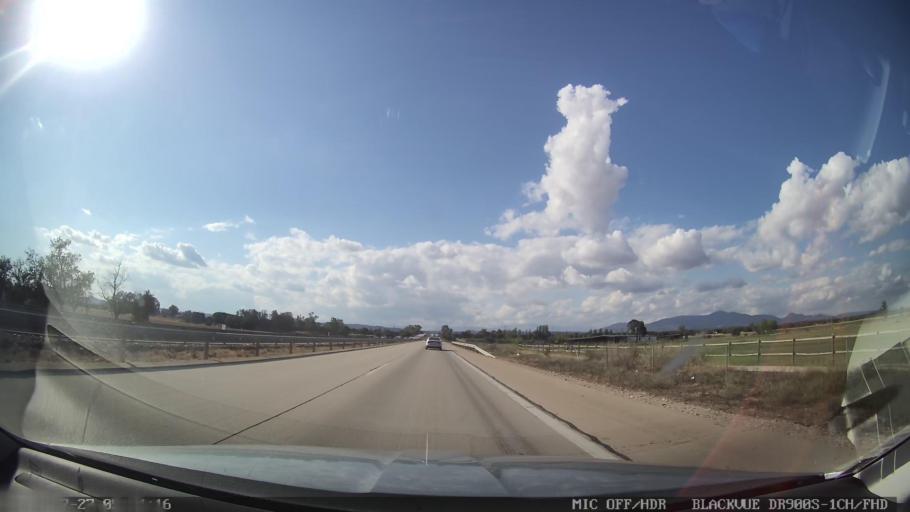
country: ES
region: Castille-La Mancha
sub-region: Province of Toledo
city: Talavera de la Reina
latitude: 39.9916
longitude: -4.7586
